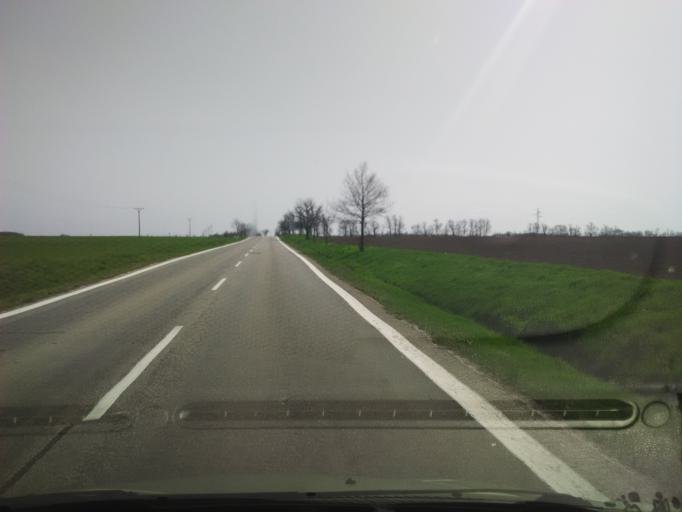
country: SK
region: Nitriansky
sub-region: Okres Nove Zamky
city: Nove Zamky
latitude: 48.0379
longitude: 18.1247
